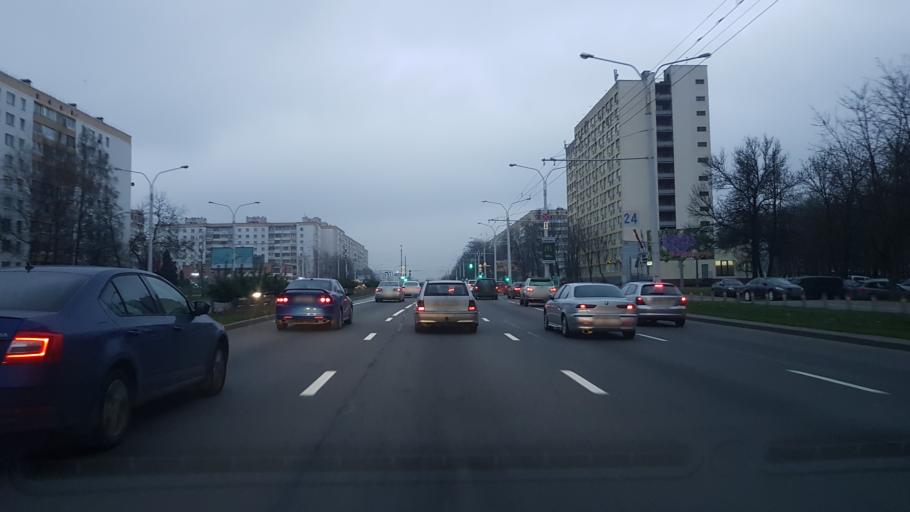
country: BY
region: Minsk
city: Novoye Medvezhino
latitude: 53.9011
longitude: 27.4969
